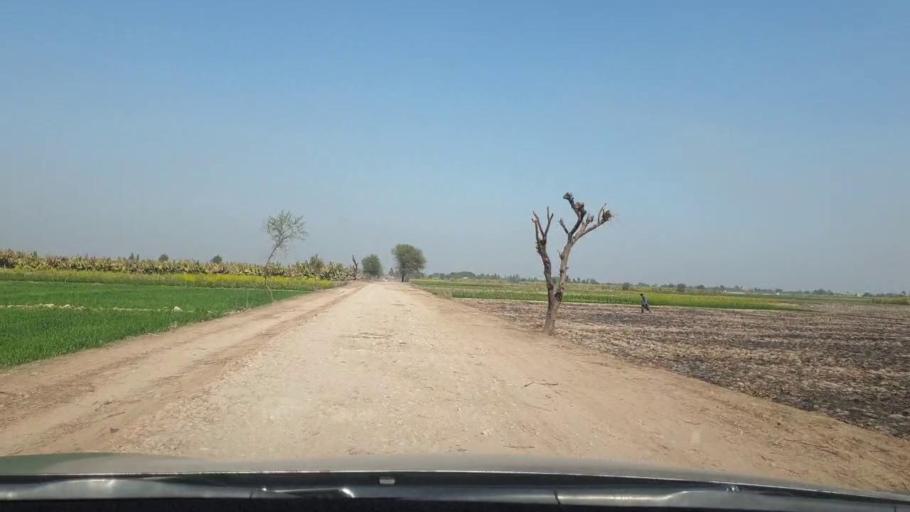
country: PK
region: Sindh
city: Tando Allahyar
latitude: 25.6013
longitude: 68.6422
